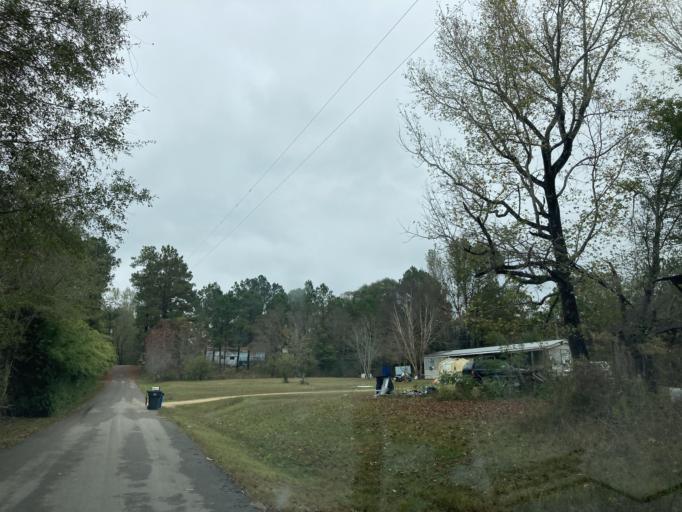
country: US
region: Mississippi
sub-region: Lamar County
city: West Hattiesburg
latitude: 31.2577
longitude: -89.5015
